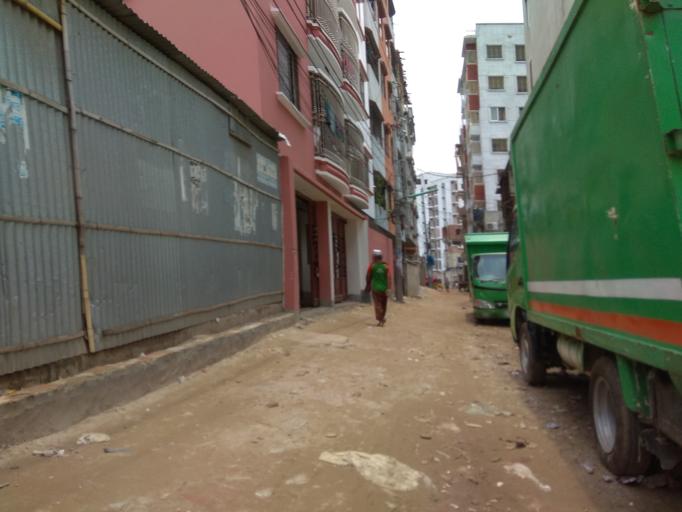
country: BD
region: Dhaka
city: Tungi
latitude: 23.8131
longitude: 90.3773
